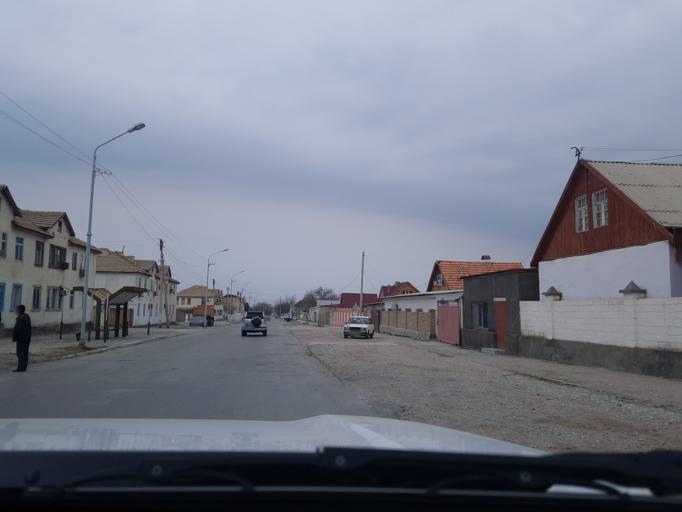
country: TM
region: Balkan
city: Balkanabat
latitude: 39.5091
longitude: 54.3770
